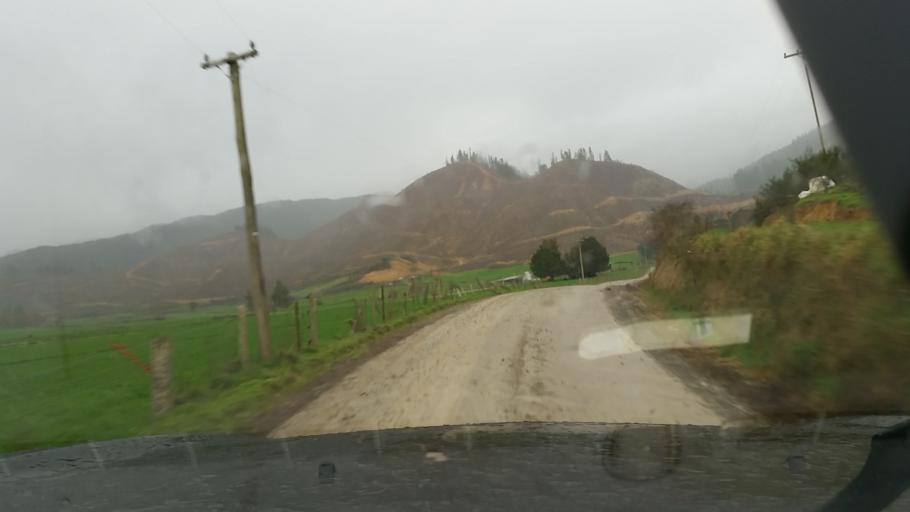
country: NZ
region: Marlborough
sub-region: Marlborough District
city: Picton
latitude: -41.3359
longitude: 173.9316
